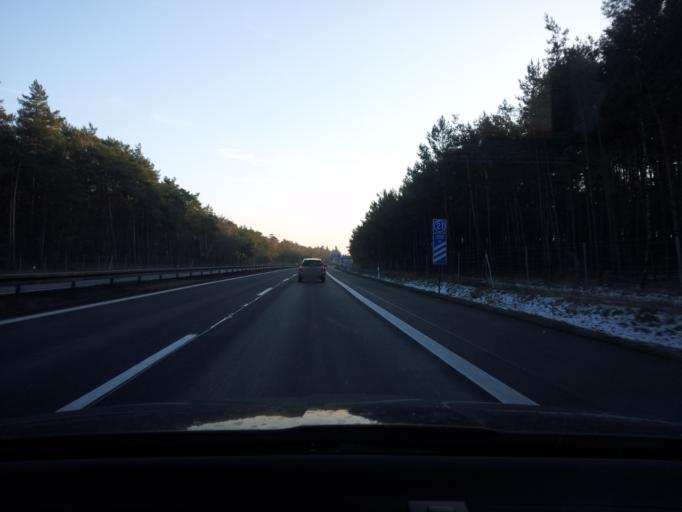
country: DE
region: Brandenburg
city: Wittstock
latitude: 53.0792
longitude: 12.5235
